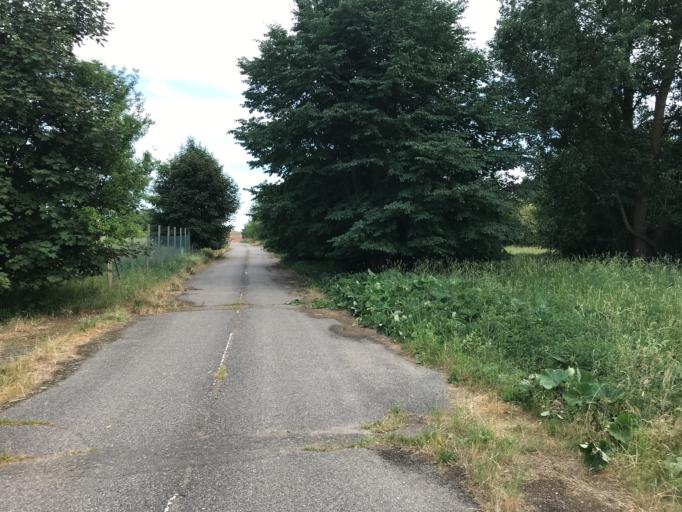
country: DK
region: Capital Region
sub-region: Ballerup Kommune
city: Malov
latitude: 55.7659
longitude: 12.3038
